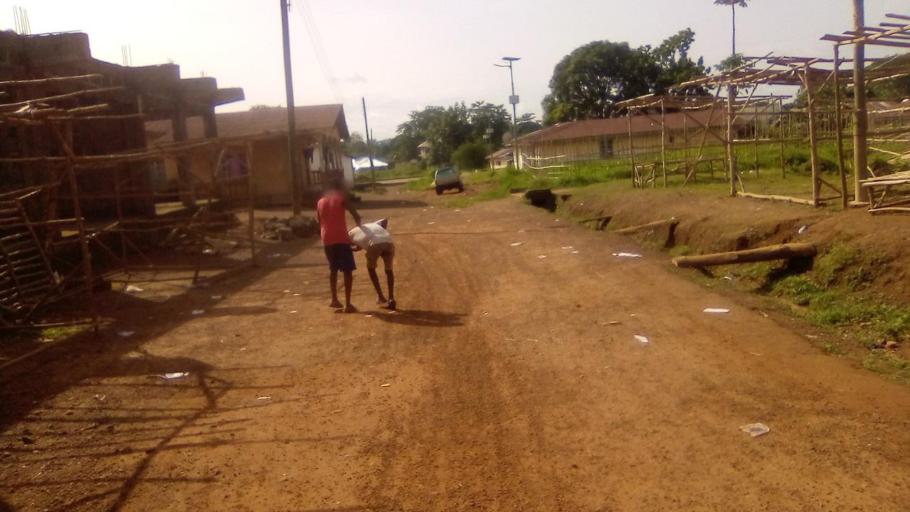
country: SL
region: Southern Province
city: Pujehun
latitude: 7.3577
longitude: -11.7204
